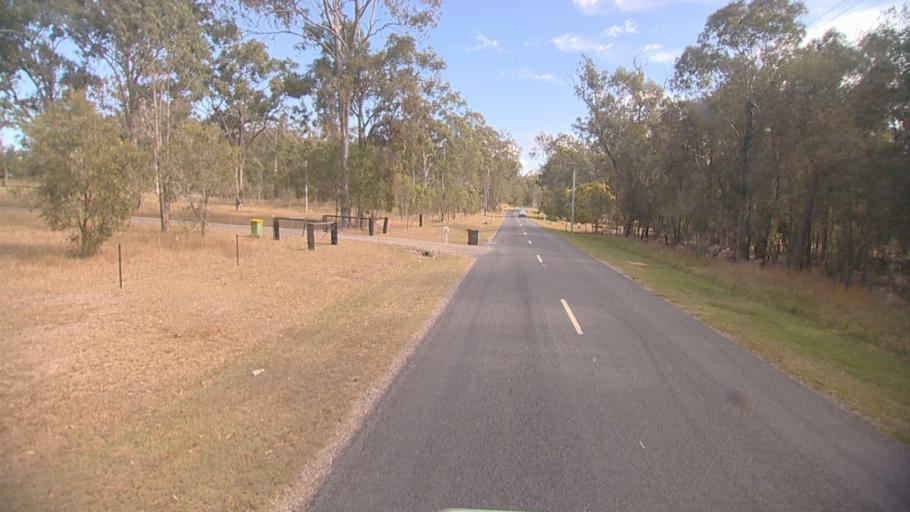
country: AU
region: Queensland
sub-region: Logan
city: North Maclean
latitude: -27.7614
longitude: 152.9751
